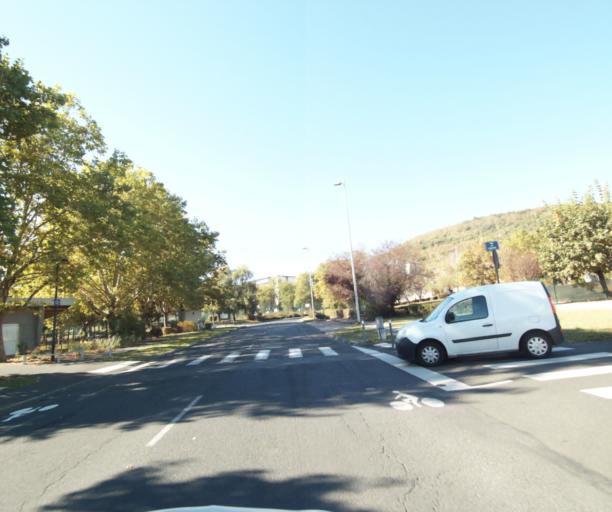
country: FR
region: Auvergne
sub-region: Departement du Puy-de-Dome
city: Cebazat
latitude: 45.8145
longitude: 3.1030
